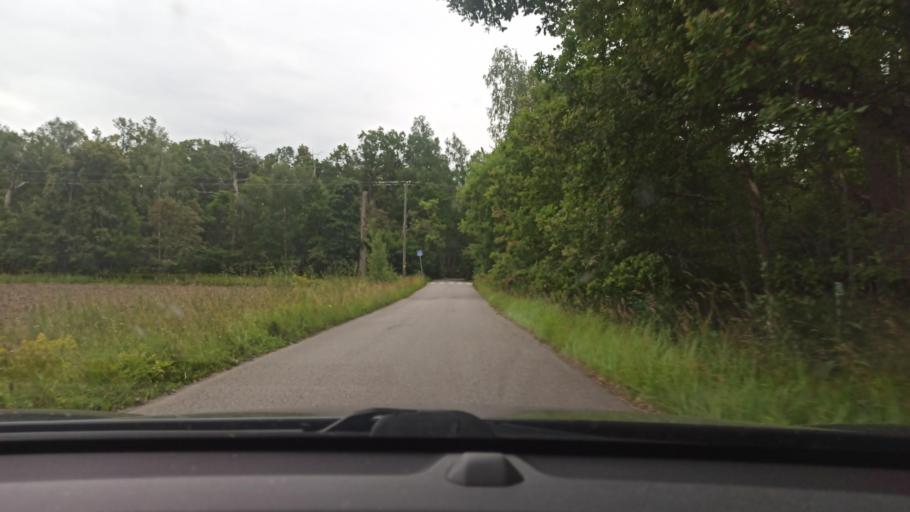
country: FI
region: Varsinais-Suomi
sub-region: Turku
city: Raisio
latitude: 60.4285
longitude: 22.1598
